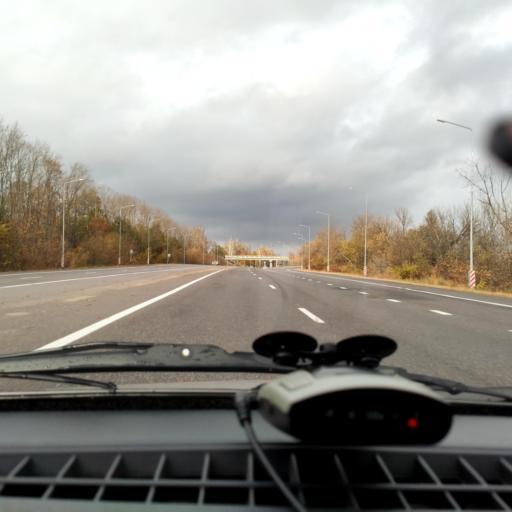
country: RU
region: Voronezj
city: Kolodeznyy
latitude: 51.3364
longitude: 39.0244
